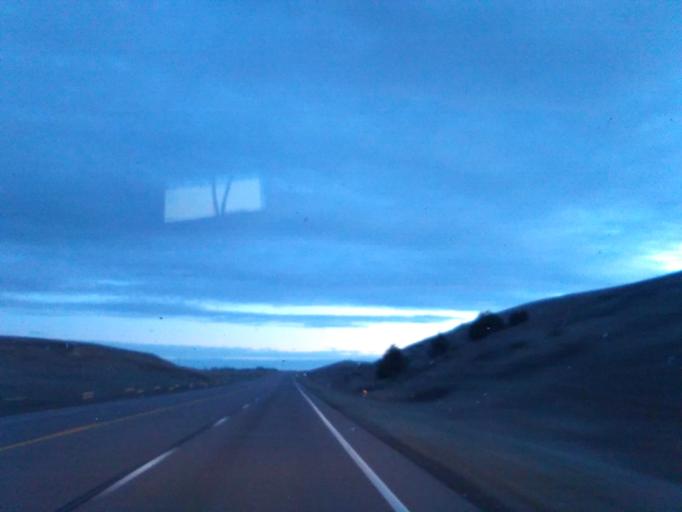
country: US
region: Nebraska
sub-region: Garden County
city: Oshkosh
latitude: 41.2493
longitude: -102.1026
